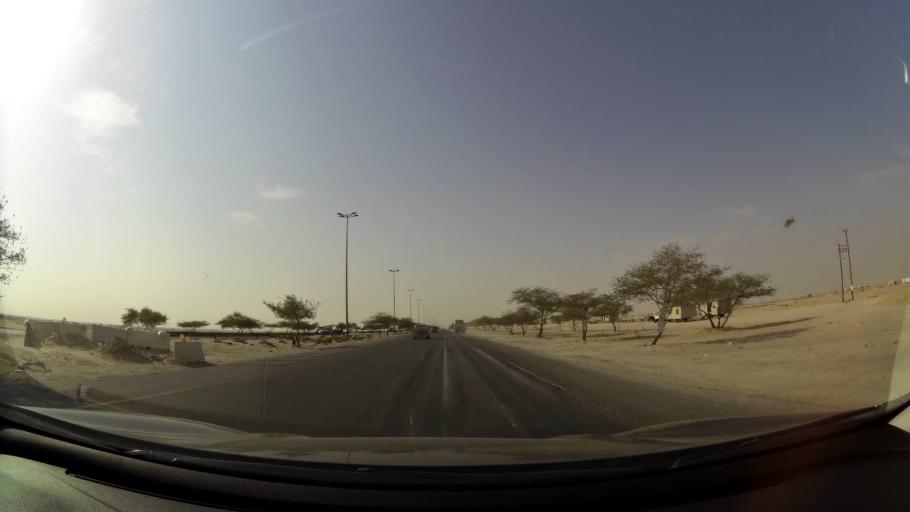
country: KW
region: Al Ahmadi
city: Al Ahmadi
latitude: 28.9303
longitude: 48.1067
